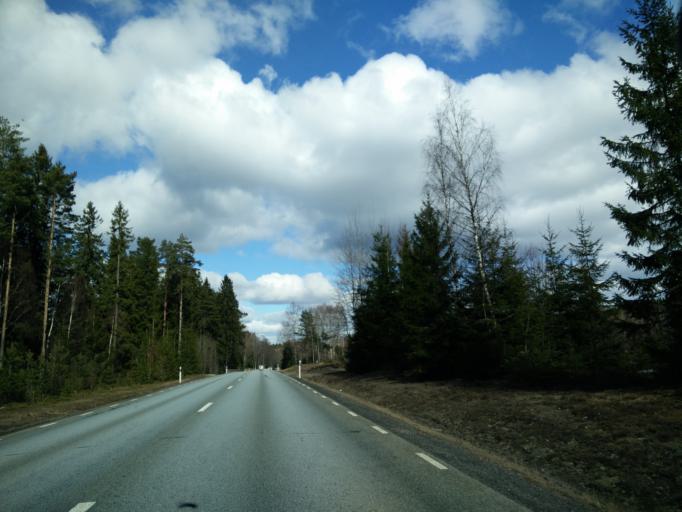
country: SE
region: Vaermland
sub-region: Hagfors Kommun
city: Hagfors
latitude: 59.9809
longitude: 13.5724
